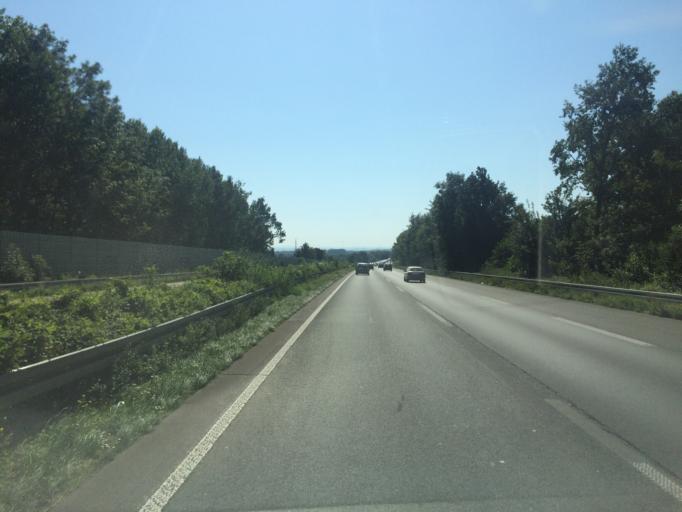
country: DE
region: North Rhine-Westphalia
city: Werne
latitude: 51.6714
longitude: 7.6809
